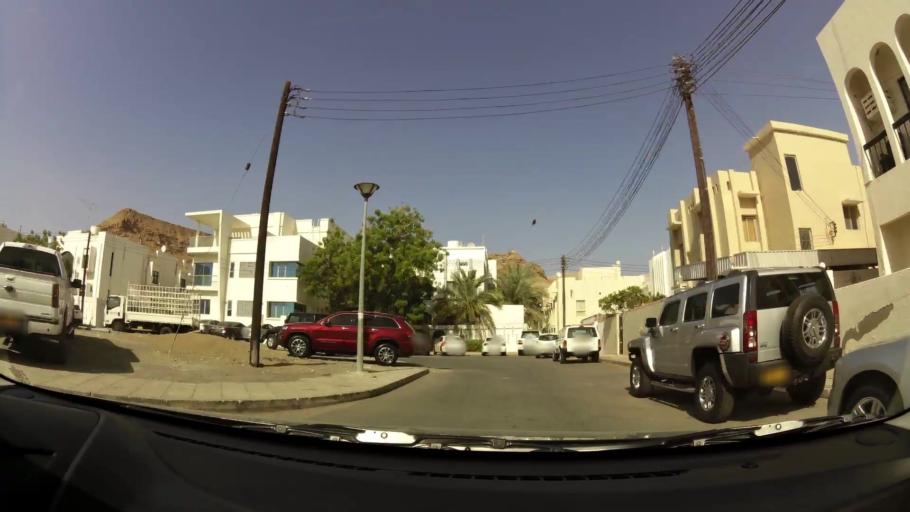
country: OM
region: Muhafazat Masqat
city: Muscat
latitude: 23.6034
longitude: 58.5120
